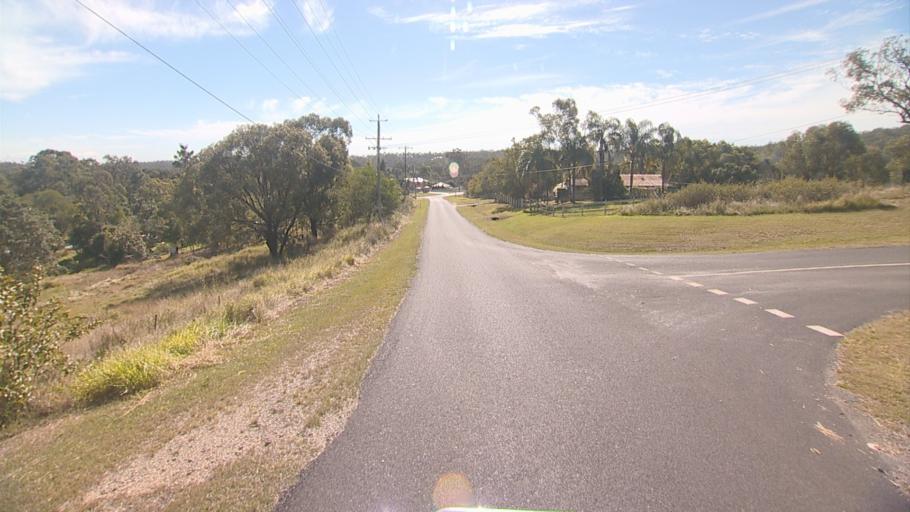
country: AU
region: Queensland
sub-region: Logan
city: Windaroo
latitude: -27.7416
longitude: 153.1730
